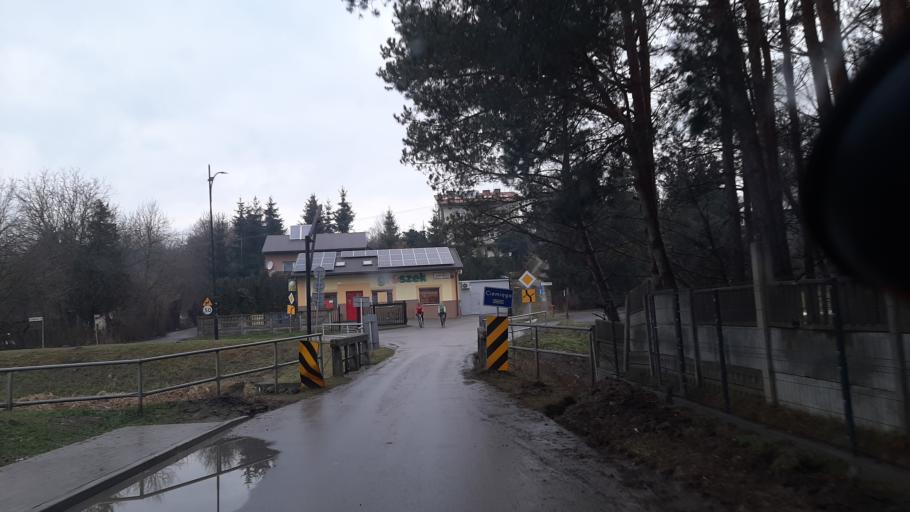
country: PL
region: Lublin Voivodeship
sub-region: Powiat lubelski
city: Lublin
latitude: 51.3148
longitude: 22.5801
